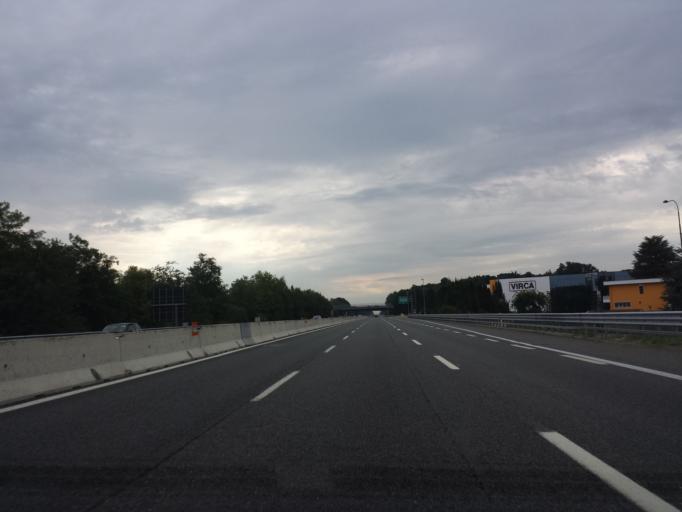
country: IT
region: Lombardy
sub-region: Provincia di Varese
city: Fagnano Olona-Bergoro
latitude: 45.6423
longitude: 8.8517
